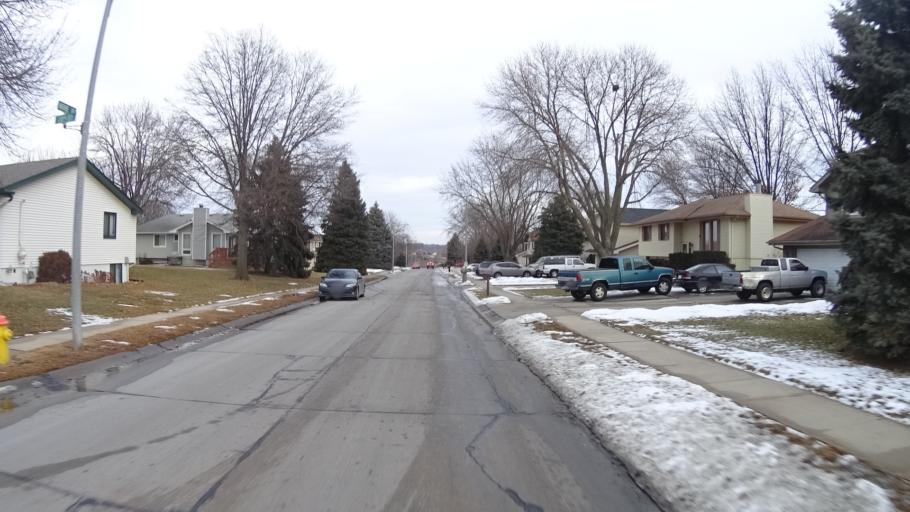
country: US
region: Nebraska
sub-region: Sarpy County
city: Offutt Air Force Base
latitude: 41.1622
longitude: -95.9460
